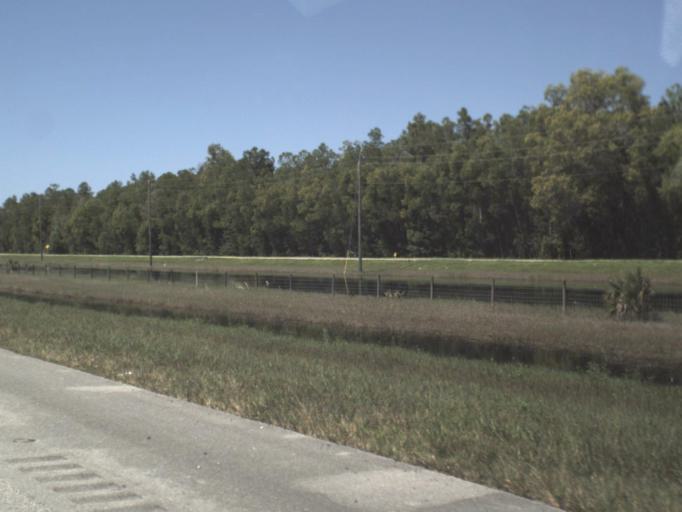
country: US
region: Florida
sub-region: Collier County
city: Golden Gate
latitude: 26.1556
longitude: -81.6668
